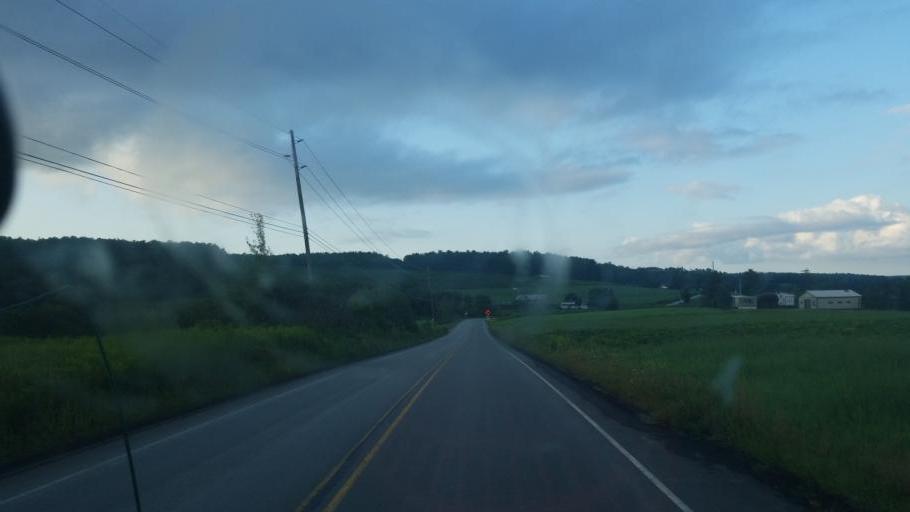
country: US
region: Pennsylvania
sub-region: Potter County
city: Galeton
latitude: 41.8592
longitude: -77.7668
